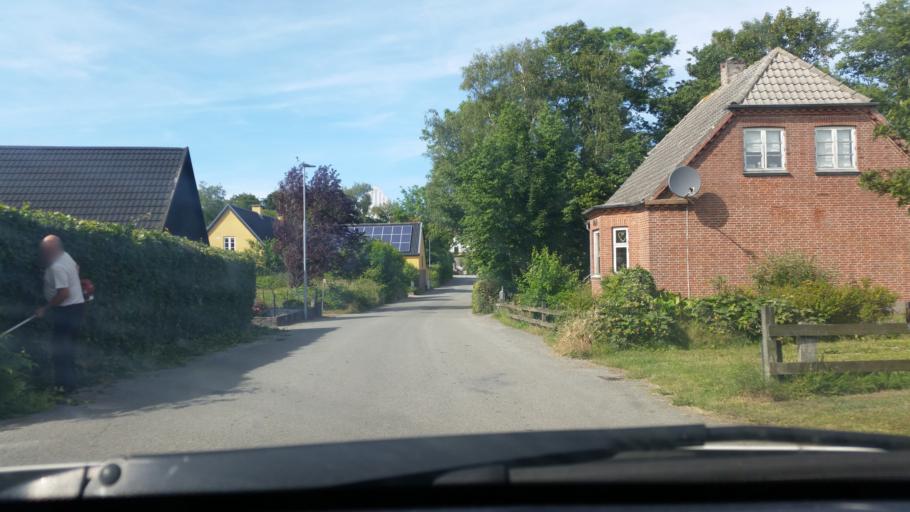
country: DK
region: Central Jutland
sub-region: Samso Kommune
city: Tranebjerg
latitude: 55.7984
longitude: 10.5564
